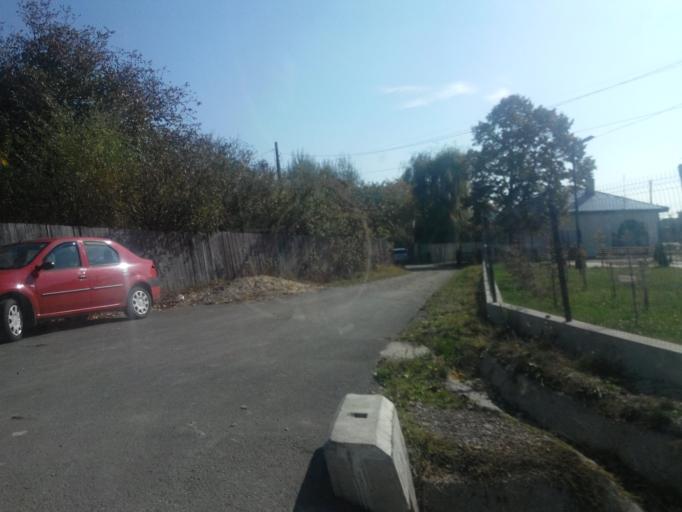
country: RO
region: Vrancea
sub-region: Comuna Bolotesti
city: Gagesti
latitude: 45.8540
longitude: 27.0564
